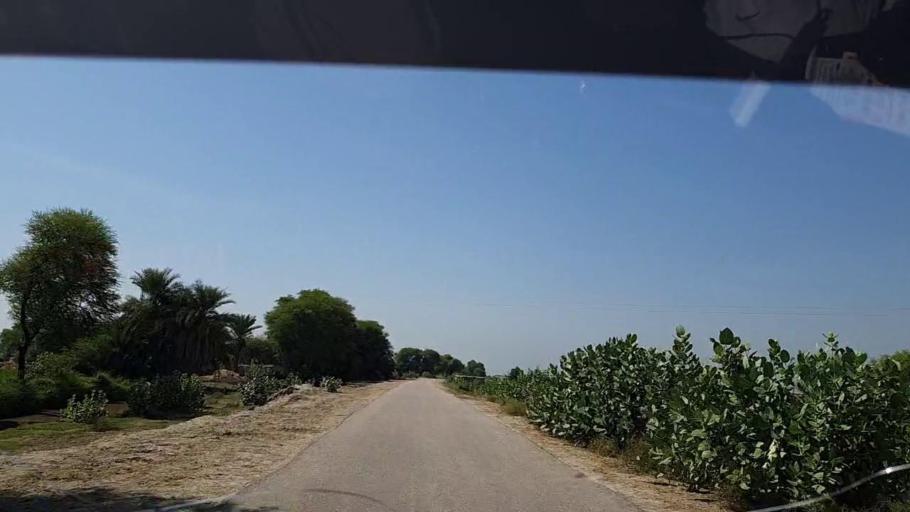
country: PK
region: Sindh
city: Kandhkot
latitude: 28.3051
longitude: 69.1115
